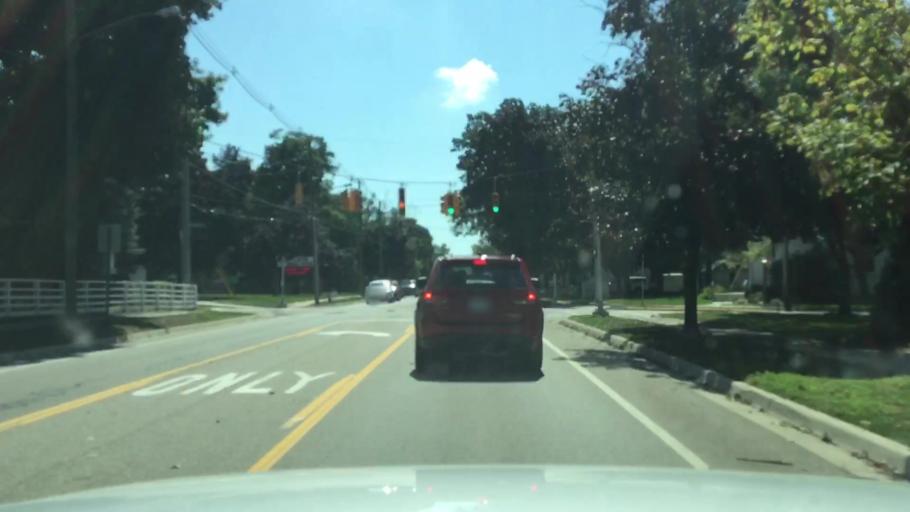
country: US
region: Michigan
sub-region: Lenawee County
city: Clinton
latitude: 42.0706
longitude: -83.9708
